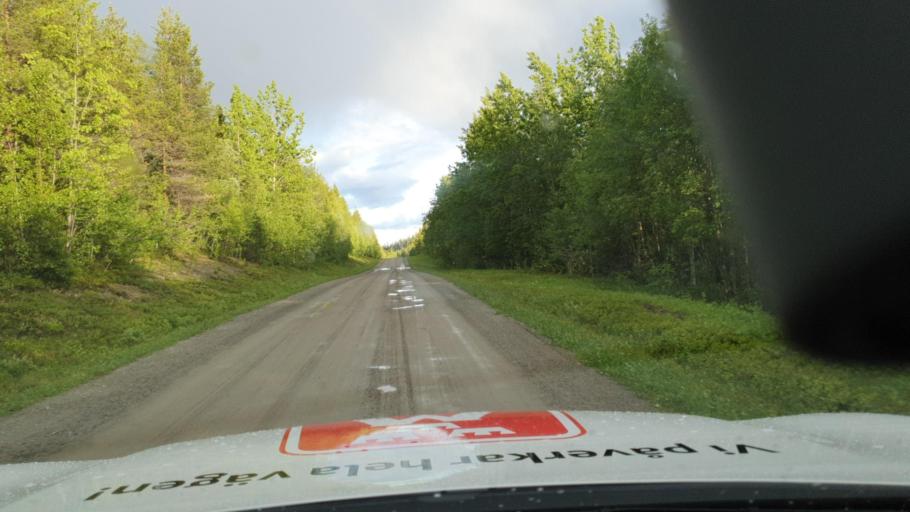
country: SE
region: Vaesterbotten
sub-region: Storumans Kommun
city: Storuman
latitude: 64.7770
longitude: 17.0373
